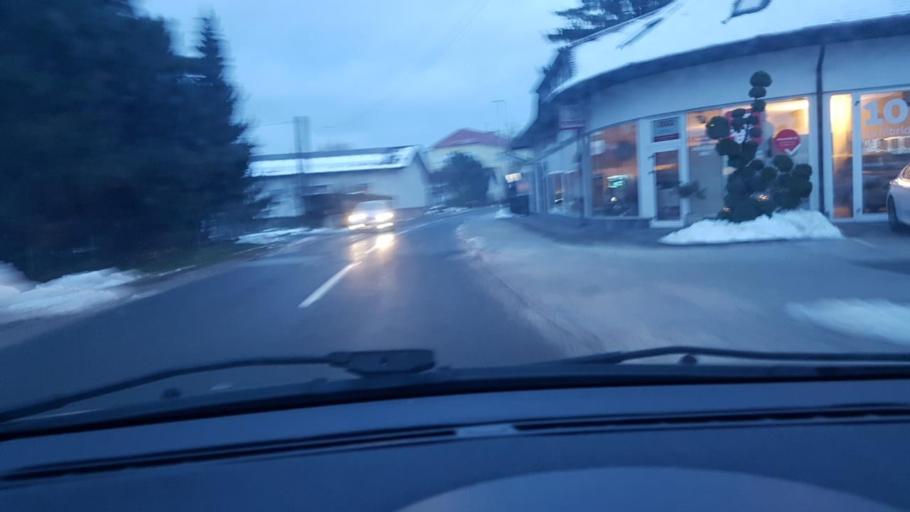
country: SI
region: Ptuj
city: Ptuj
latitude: 46.4138
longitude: 15.8609
